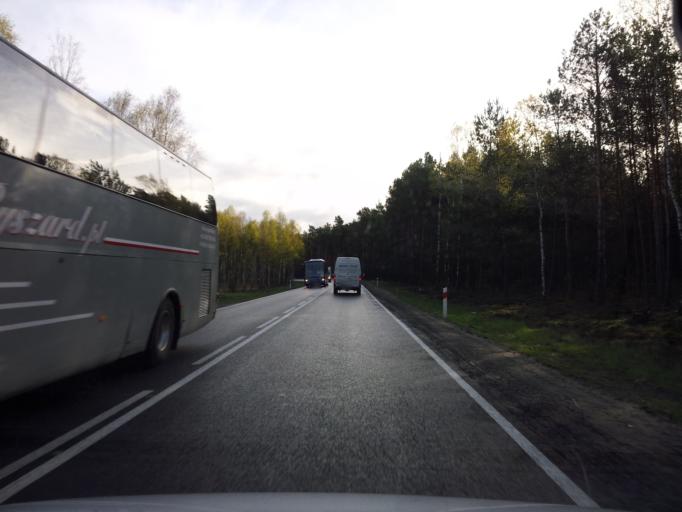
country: PL
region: Lubusz
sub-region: Powiat zielonogorski
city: Nowogrod Bobrzanski
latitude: 51.8336
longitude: 15.3171
